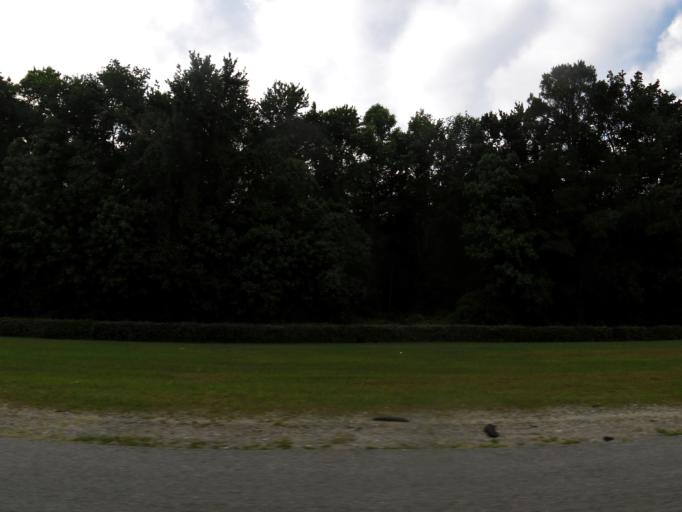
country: US
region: South Carolina
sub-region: Jasper County
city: Hardeeville
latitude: 32.2417
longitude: -81.1433
